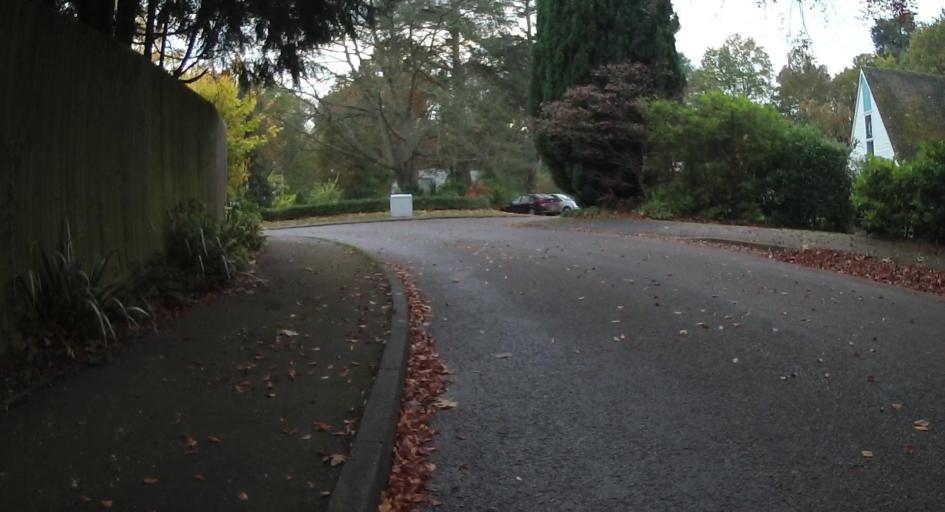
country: GB
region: England
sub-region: Bracknell Forest
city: Crowthorne
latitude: 51.3751
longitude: -0.8103
